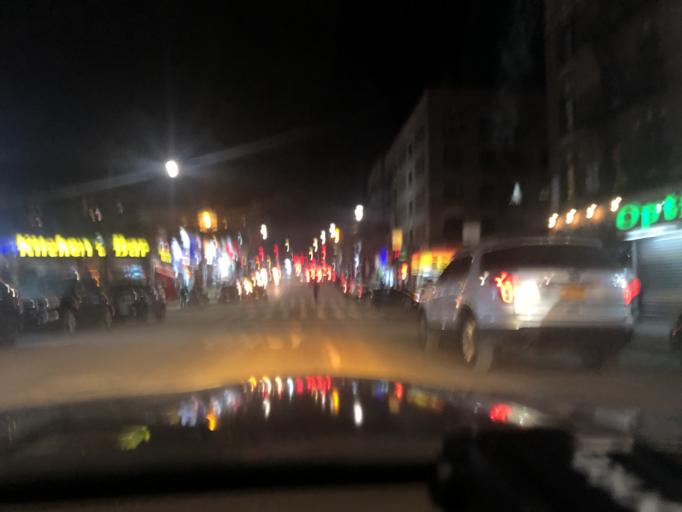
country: US
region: New York
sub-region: New York County
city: Inwood
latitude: 40.8665
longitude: -73.9204
